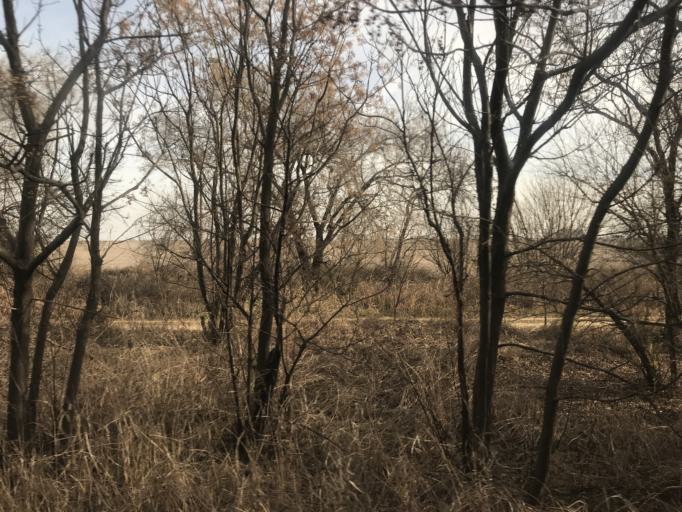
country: AR
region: Cordoba
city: Laguna Larga
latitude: -31.7358
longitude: -63.8390
